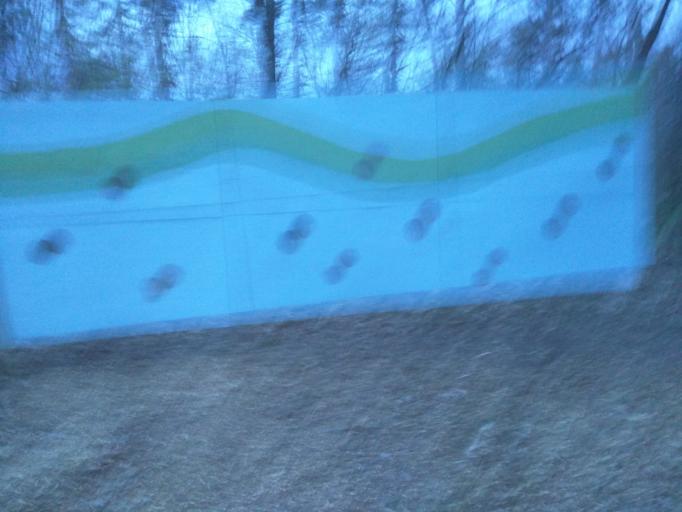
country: US
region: Michigan
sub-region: Ingham County
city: Lansing
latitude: 42.7106
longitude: -84.5204
